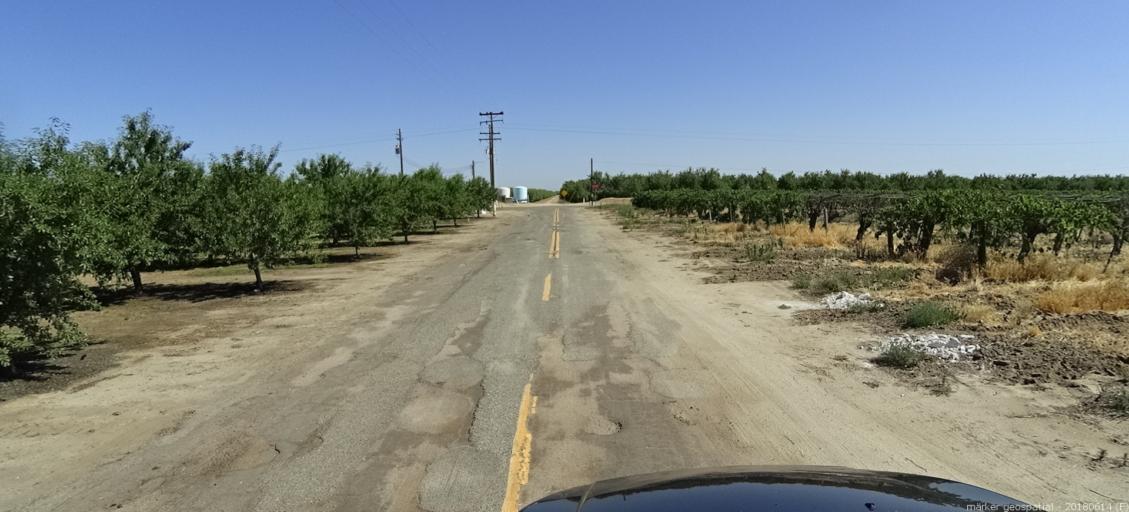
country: US
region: California
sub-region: Madera County
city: Madera
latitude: 36.9813
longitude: -120.1380
